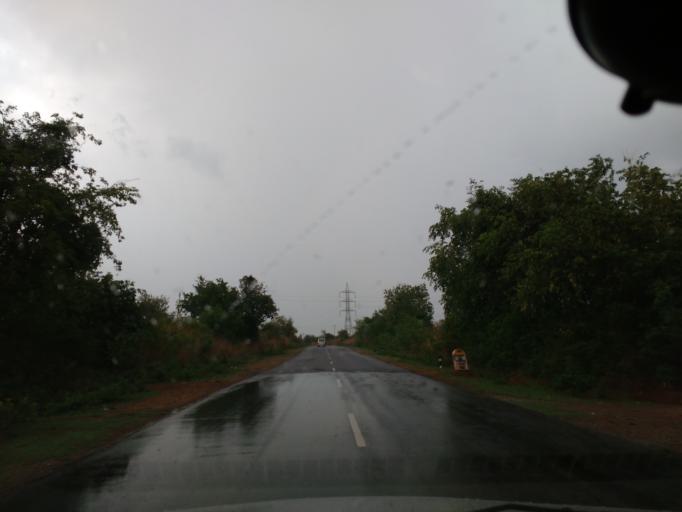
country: IN
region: Karnataka
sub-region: Tumkur
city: Tiptur
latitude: 13.2914
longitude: 76.5765
